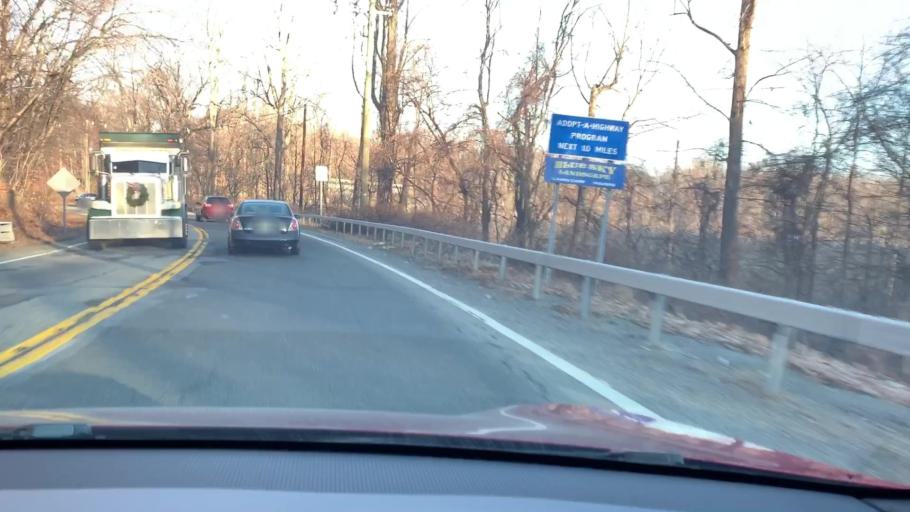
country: US
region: New York
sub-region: Rockland County
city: Sparkill
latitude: 41.0022
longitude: -73.9119
